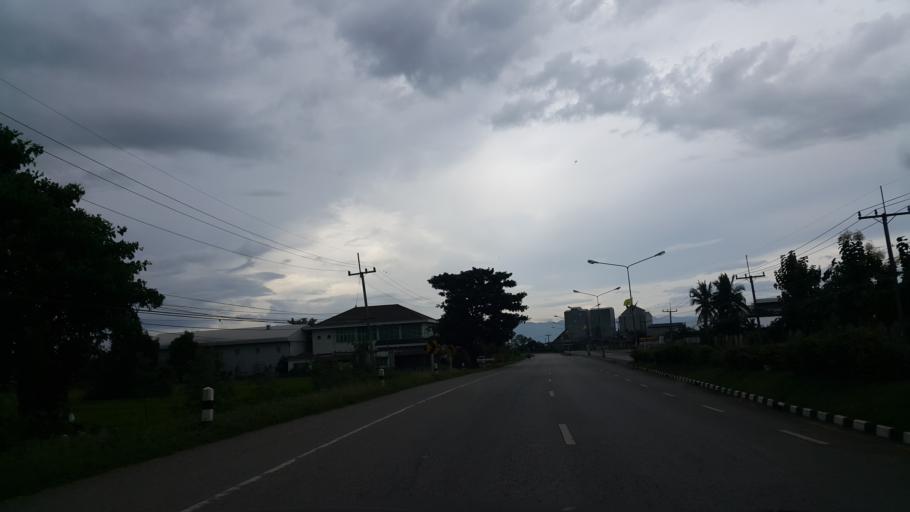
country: TH
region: Phayao
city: Dok Kham Tai
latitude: 19.1549
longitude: 99.9426
